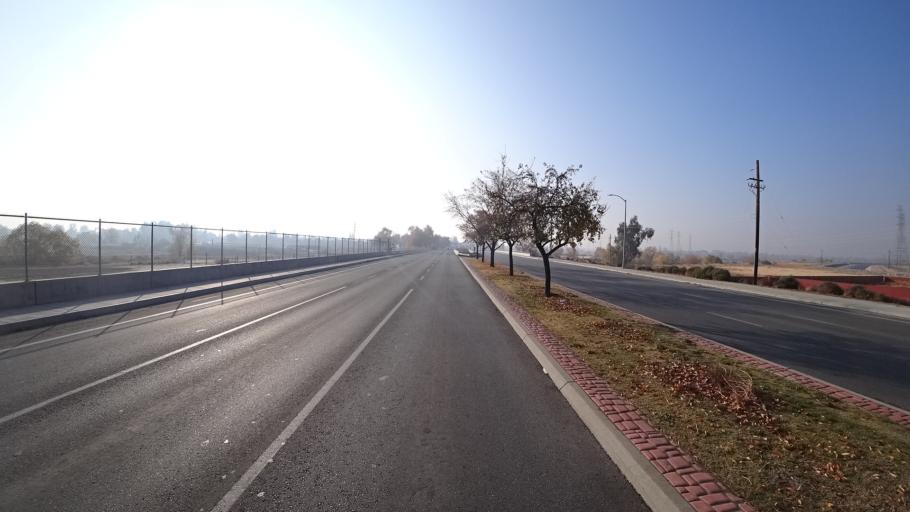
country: US
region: California
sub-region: Kern County
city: Greenacres
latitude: 35.3648
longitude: -119.0918
